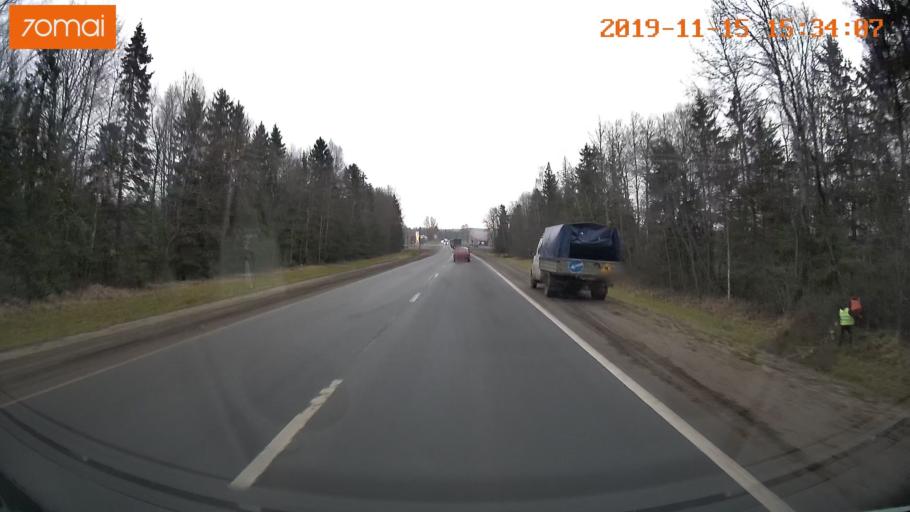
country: RU
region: Jaroslavl
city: Danilov
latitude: 58.0729
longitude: 40.0900
